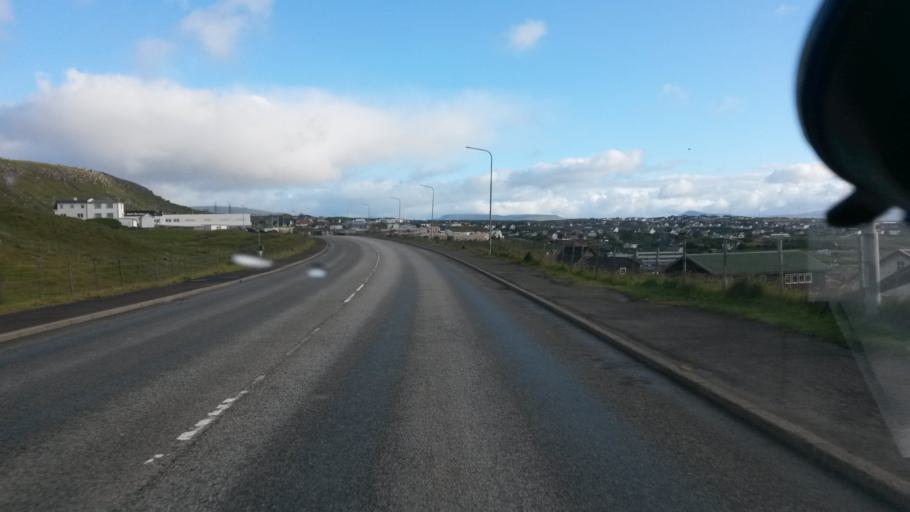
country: FO
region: Streymoy
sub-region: Torshavn
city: Torshavn
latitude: 62.0170
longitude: -6.7881
